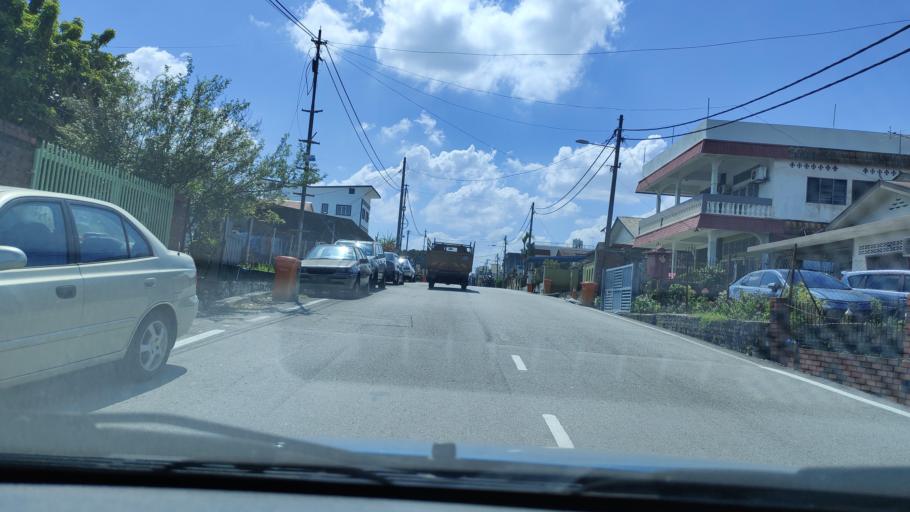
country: MY
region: Selangor
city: Kampong Baharu Balakong
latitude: 3.0227
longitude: 101.7035
